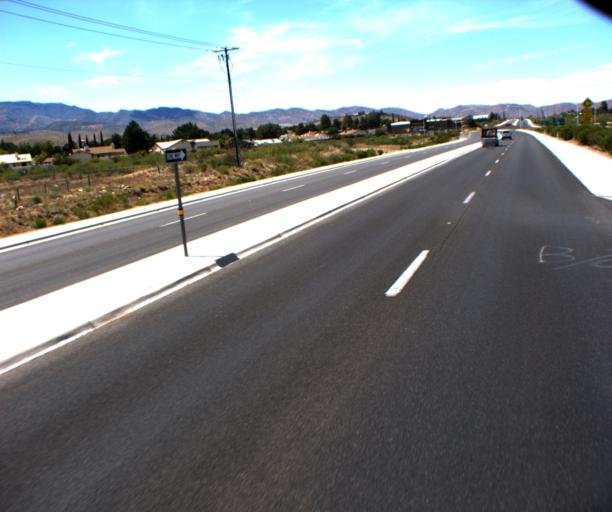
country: US
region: Arizona
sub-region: Yavapai County
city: Clarkdale
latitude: 34.7527
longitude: -112.0517
